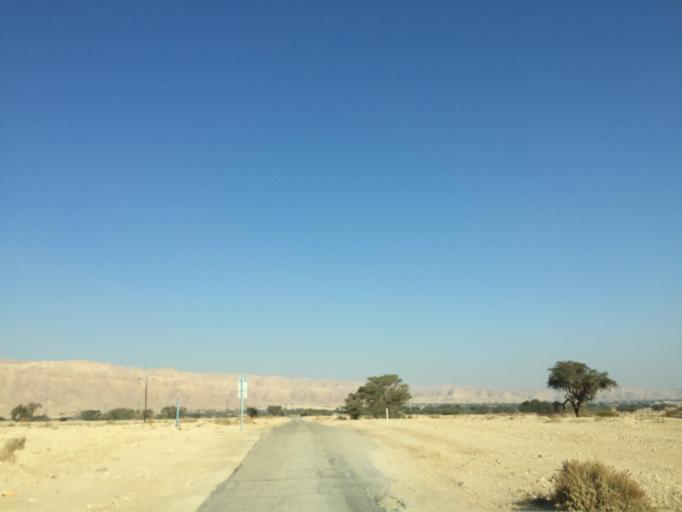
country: JO
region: Ma'an
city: Al Quwayrah
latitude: 29.8402
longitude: 35.0304
